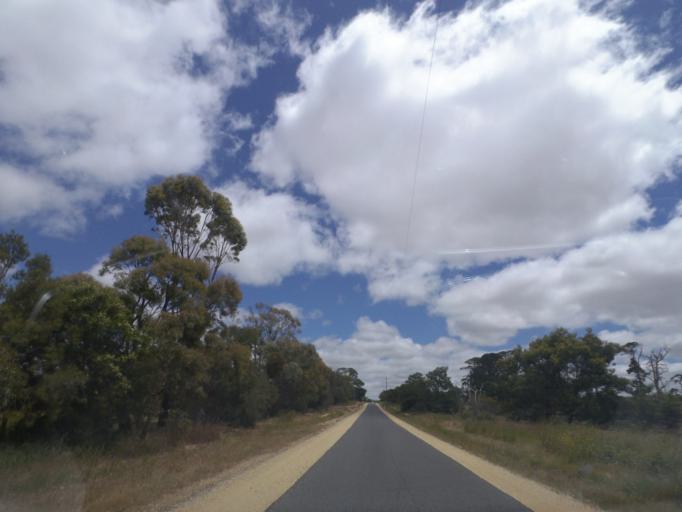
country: AU
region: Victoria
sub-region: Moorabool
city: Bacchus Marsh
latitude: -37.6519
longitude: 144.3129
